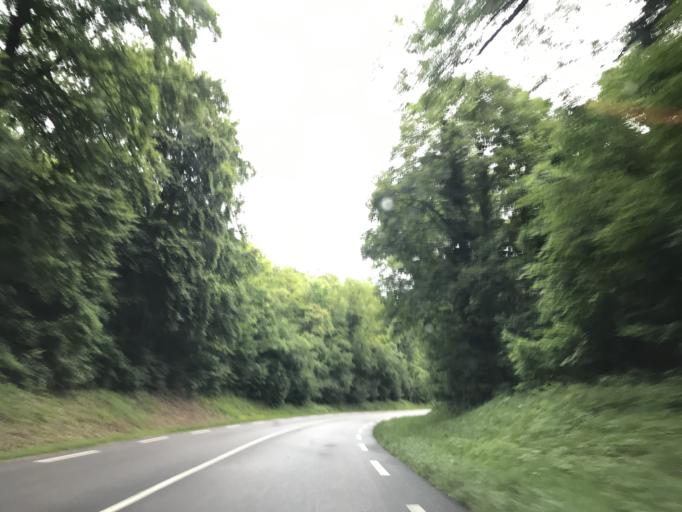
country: FR
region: Ile-de-France
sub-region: Departement des Yvelines
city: Bennecourt
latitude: 49.0304
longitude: 1.5542
